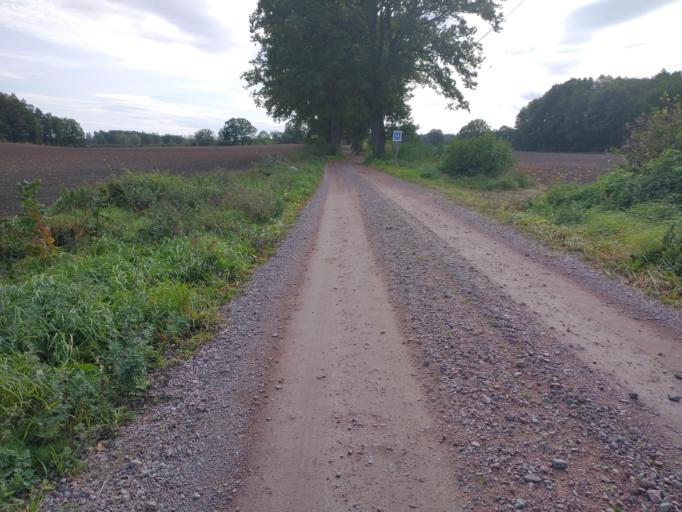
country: SE
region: Kalmar
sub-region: Kalmar Kommun
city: Lindsdal
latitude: 56.7759
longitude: 16.3079
